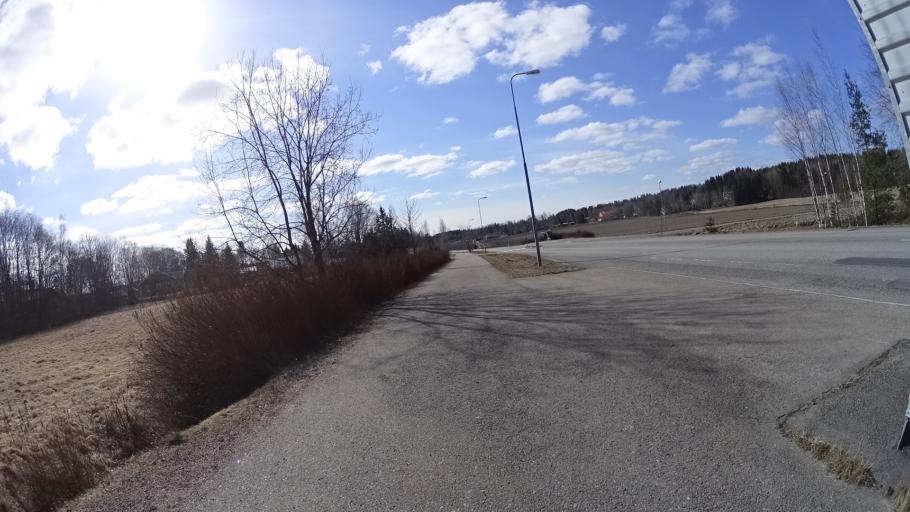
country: FI
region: Uusimaa
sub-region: Helsinki
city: Kauniainen
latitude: 60.2598
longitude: 24.7348
